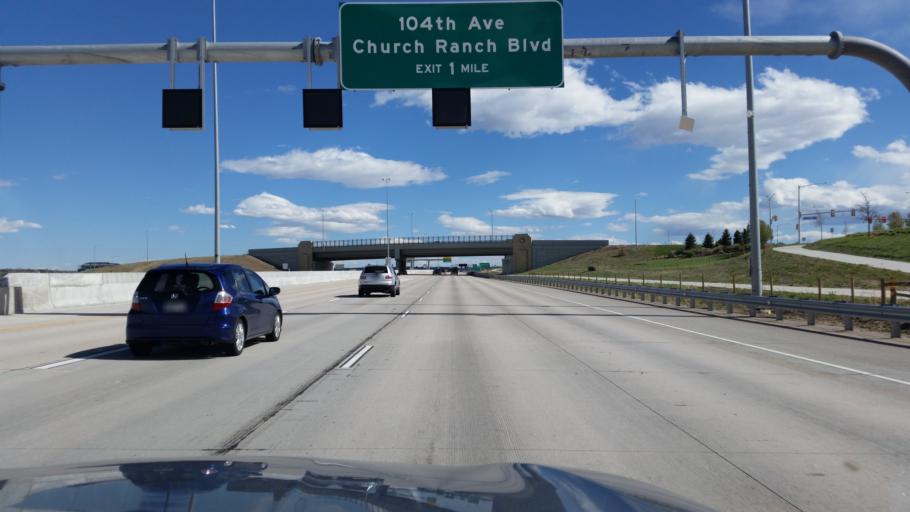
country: US
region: Colorado
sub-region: Broomfield County
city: Broomfield
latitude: 39.9034
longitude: -105.0830
